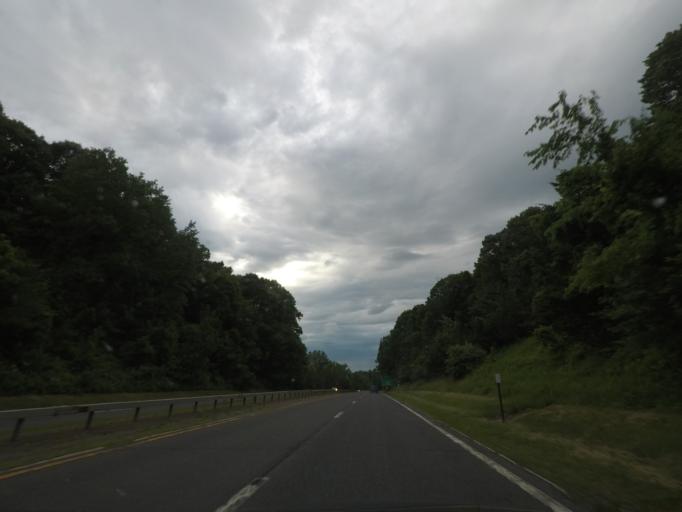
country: US
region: New York
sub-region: Dutchess County
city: Pine Plains
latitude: 42.0045
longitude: -73.7382
